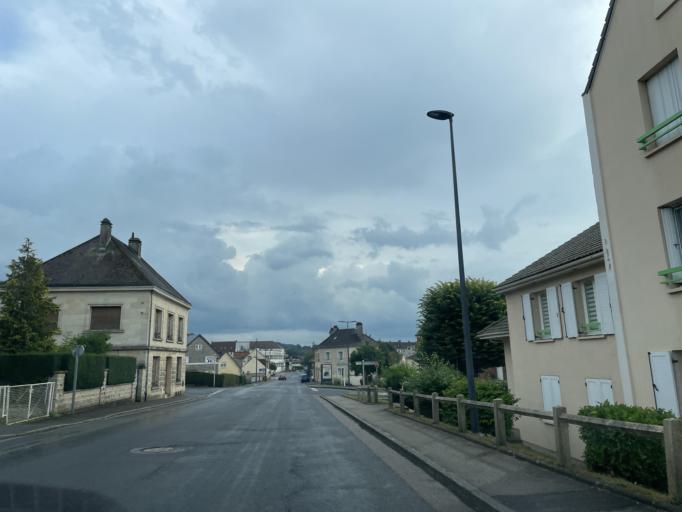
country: FR
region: Haute-Normandie
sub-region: Departement de la Seine-Maritime
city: Neufchatel-en-Bray
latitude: 49.7338
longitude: 1.4370
